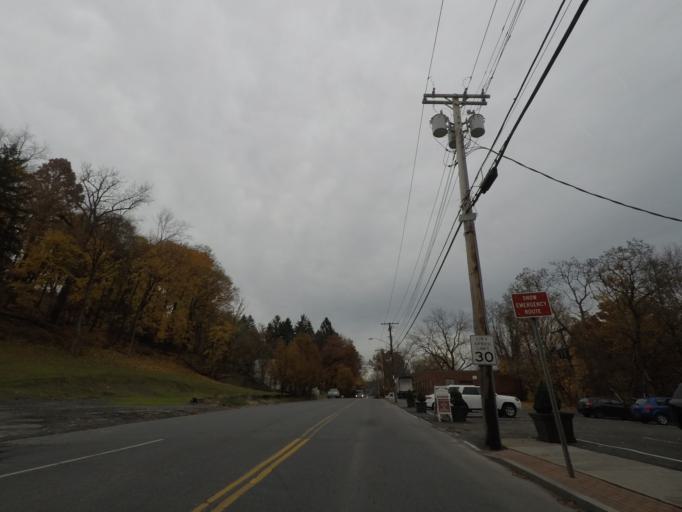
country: US
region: New York
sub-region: Rensselaer County
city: Troy
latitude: 42.7223
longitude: -73.6741
